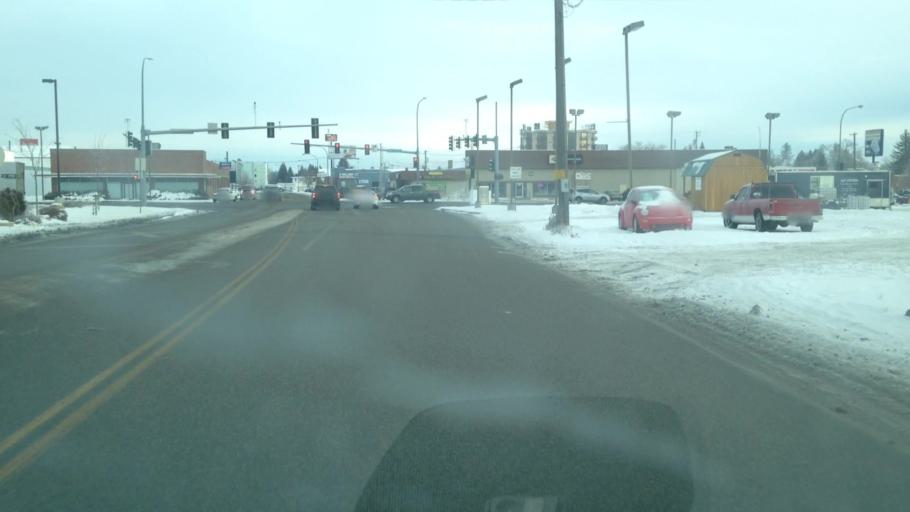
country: US
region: Idaho
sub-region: Bonneville County
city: Idaho Falls
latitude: 43.4937
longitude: -112.0487
